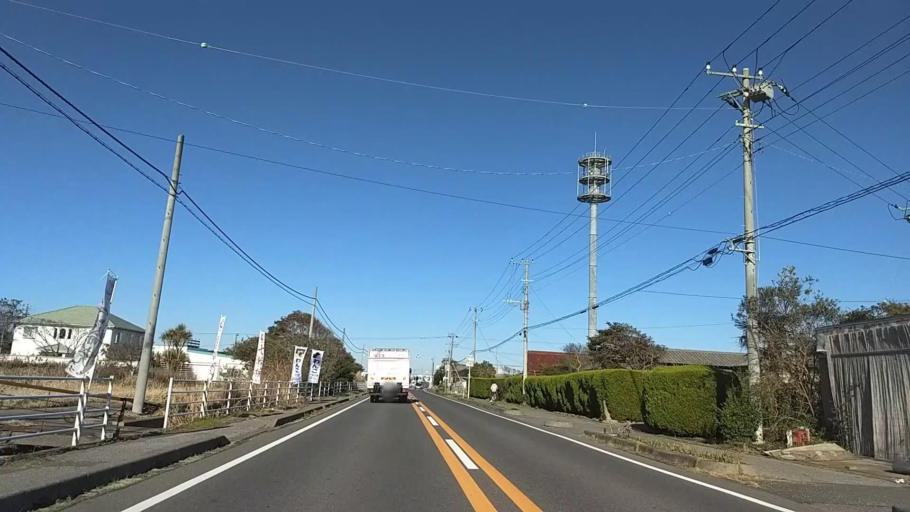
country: JP
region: Chiba
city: Togane
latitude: 35.4940
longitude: 140.4250
